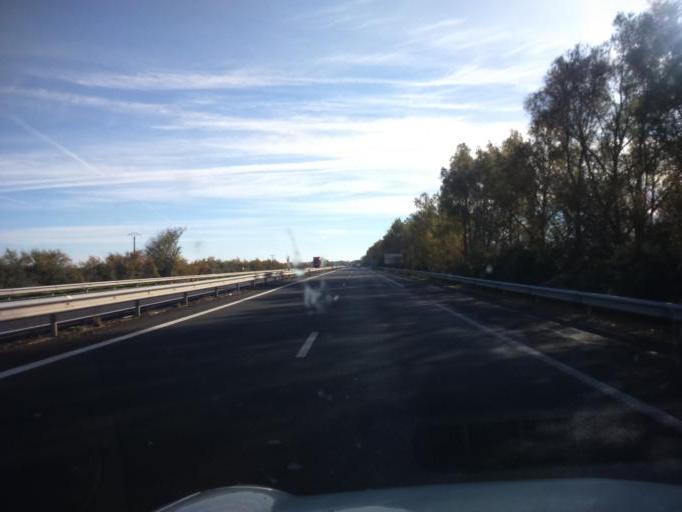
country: FR
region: Poitou-Charentes
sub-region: Departement de la Charente-Maritime
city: Breuil-Magne
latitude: 45.9600
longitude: -0.9496
